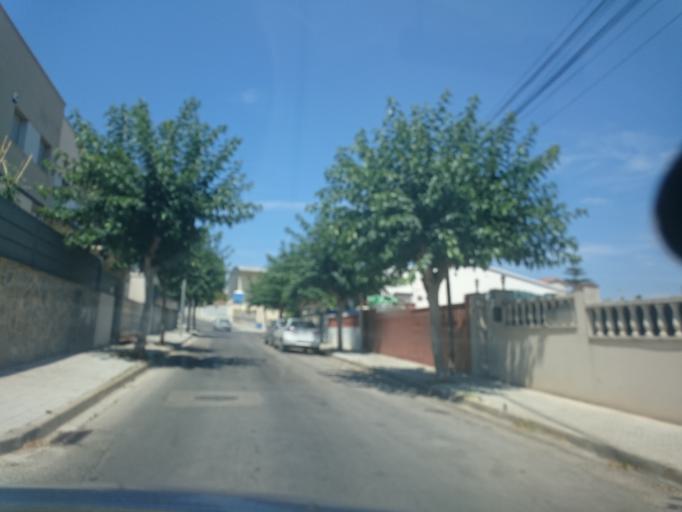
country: ES
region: Catalonia
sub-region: Provincia de Barcelona
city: Vilanova i la Geltru
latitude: 41.2252
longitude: 1.6963
